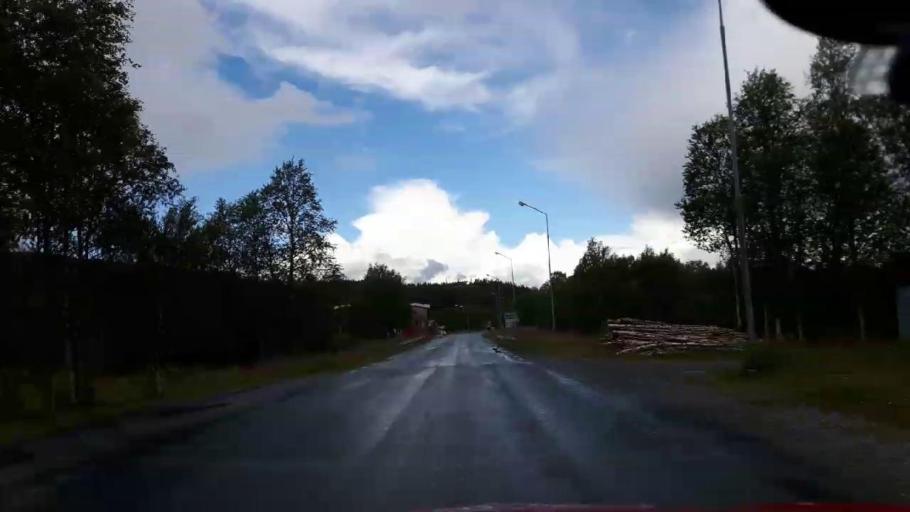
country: SE
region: Vaesterbotten
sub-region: Vilhelmina Kommun
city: Sjoberg
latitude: 64.9720
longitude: 15.3367
